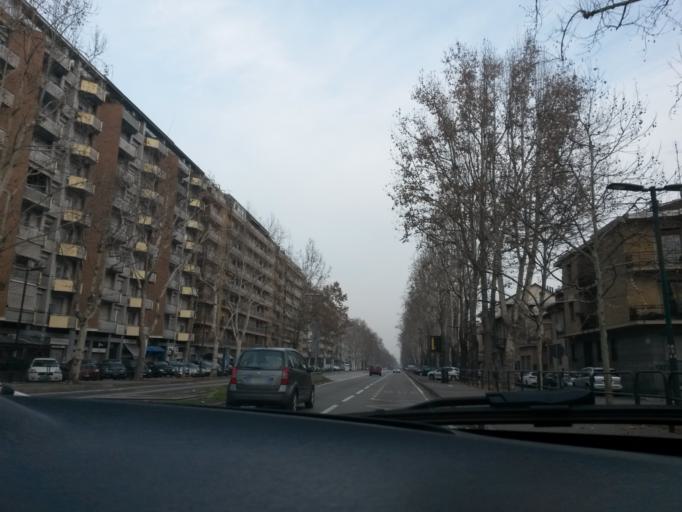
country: IT
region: Piedmont
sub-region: Provincia di Torino
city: Lesna
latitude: 45.0747
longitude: 7.6245
